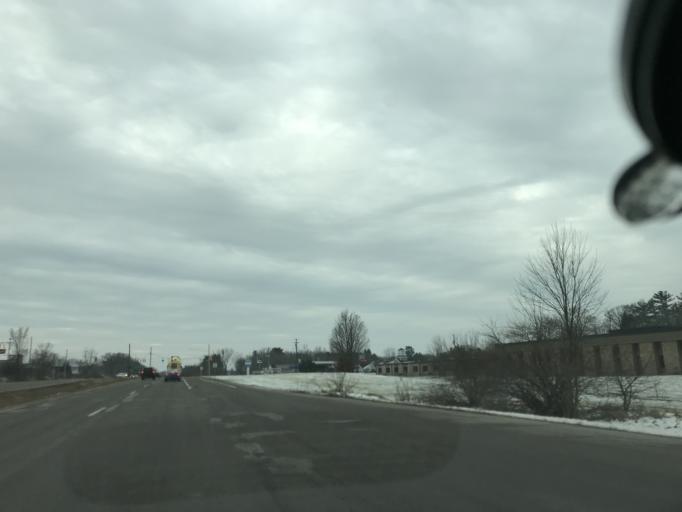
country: US
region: Michigan
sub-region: Kent County
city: Rockford
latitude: 43.1193
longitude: -85.5481
